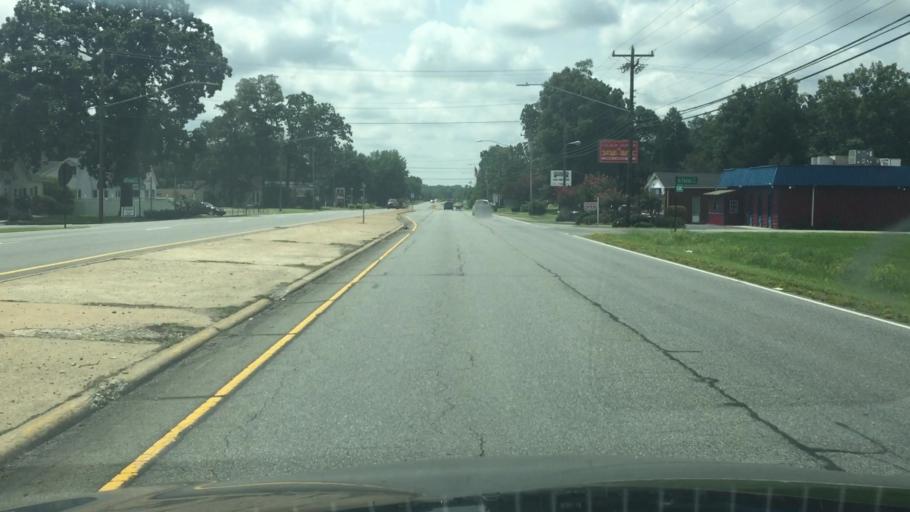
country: US
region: North Carolina
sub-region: Cabarrus County
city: Kannapolis
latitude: 35.4636
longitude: -80.6094
